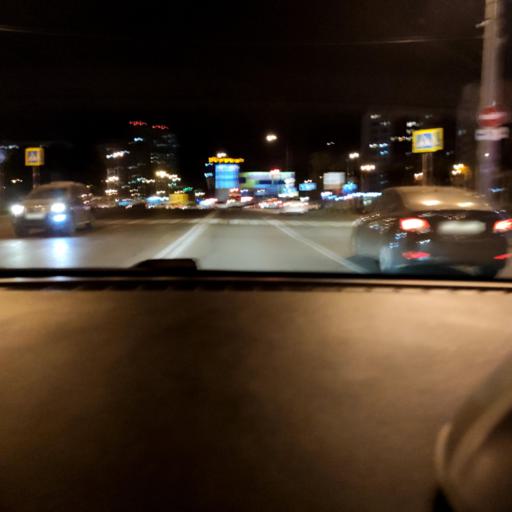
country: RU
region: Samara
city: Samara
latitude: 53.2593
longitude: 50.2121
